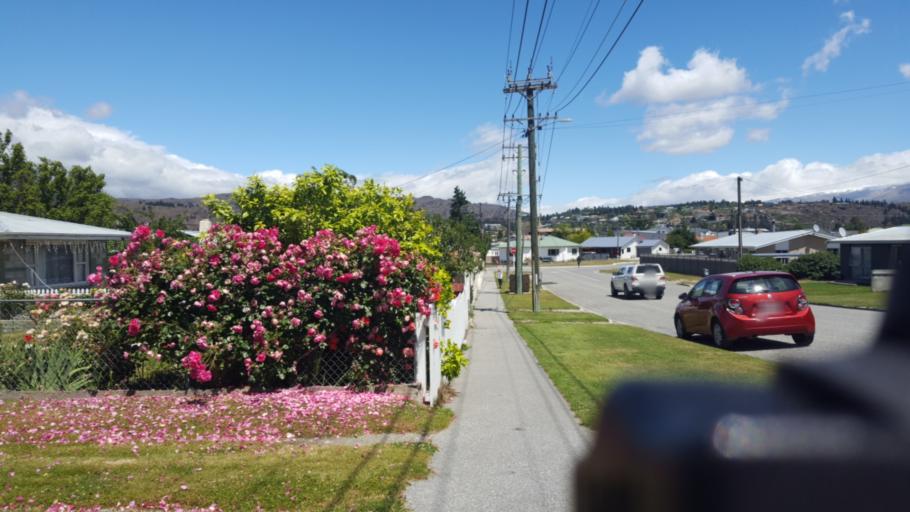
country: NZ
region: Otago
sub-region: Queenstown-Lakes District
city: Wanaka
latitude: -45.2474
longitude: 169.3892
